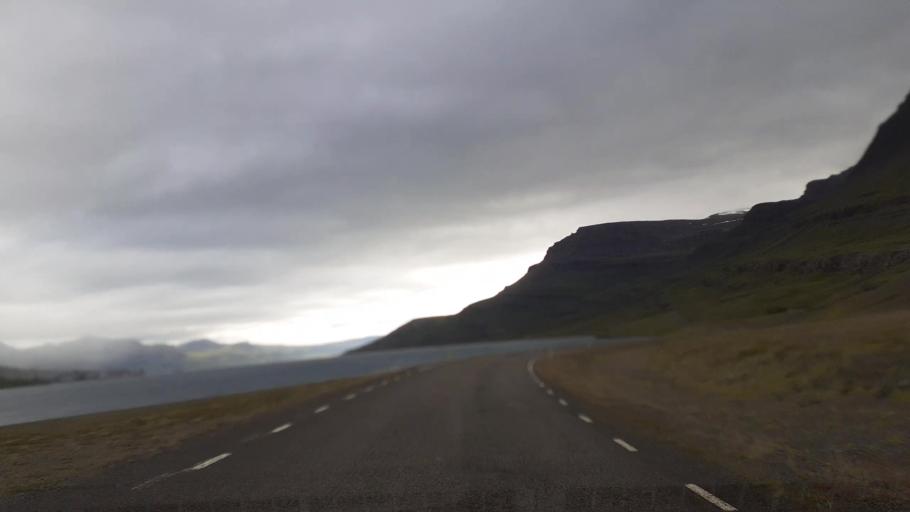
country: IS
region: East
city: Reydarfjoerdur
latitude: 65.0171
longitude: -14.2046
